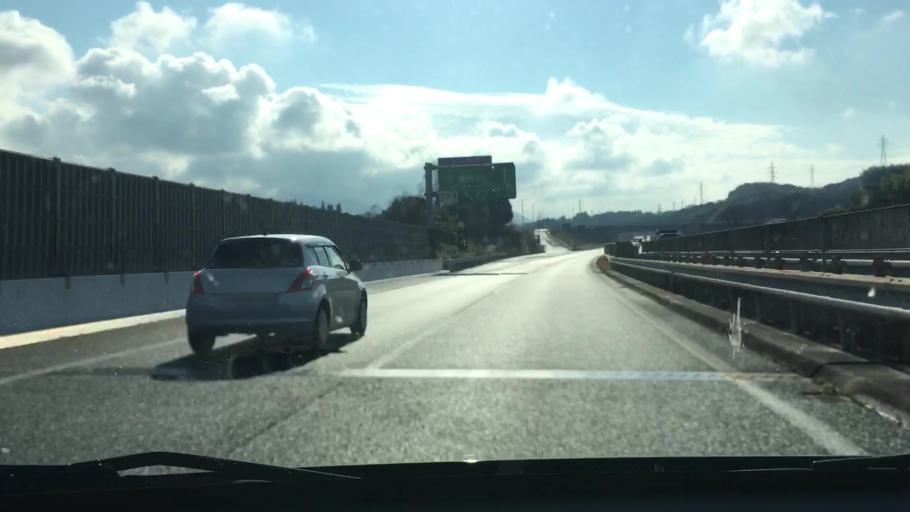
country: JP
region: Kumamoto
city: Matsubase
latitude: 32.5801
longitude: 130.7137
